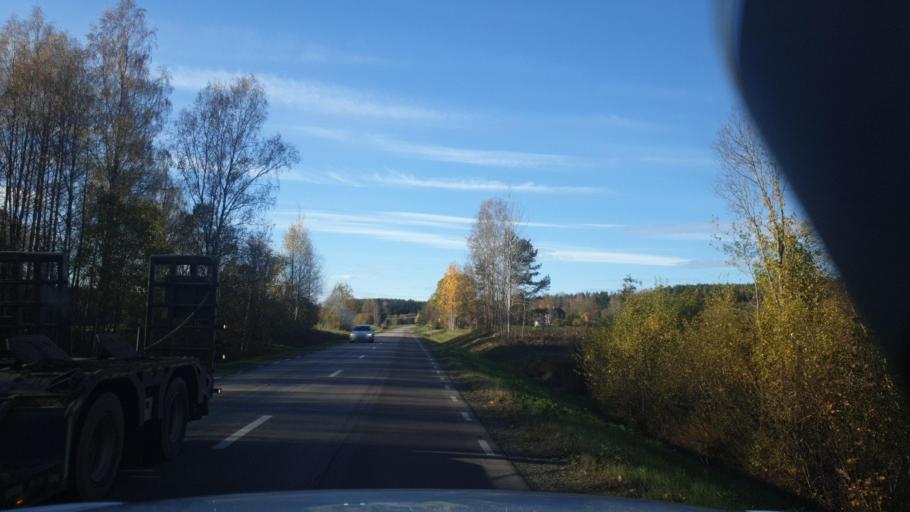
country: SE
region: Vaermland
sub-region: Arvika Kommun
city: Arvika
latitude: 59.6340
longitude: 12.8043
